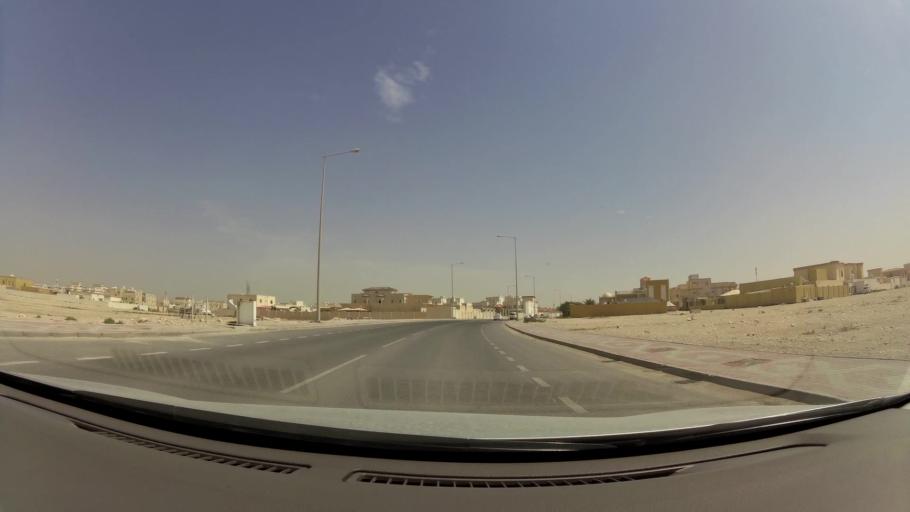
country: QA
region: Baladiyat ar Rayyan
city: Ar Rayyan
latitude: 25.2559
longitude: 51.4062
